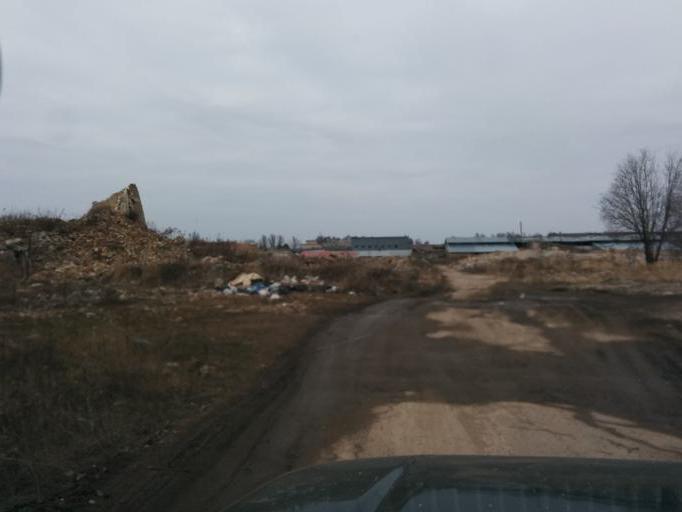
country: LV
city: Tireli
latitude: 56.9429
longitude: 23.6346
